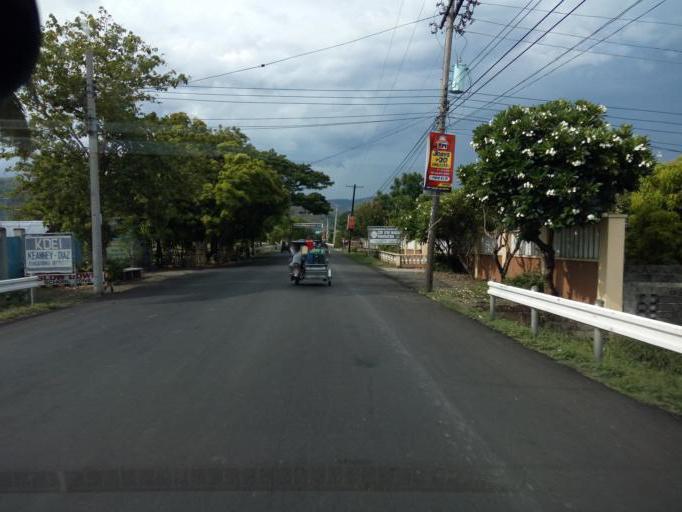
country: PH
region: Central Luzon
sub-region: Province of Nueva Ecija
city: Sibul
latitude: 15.8190
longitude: 121.0069
